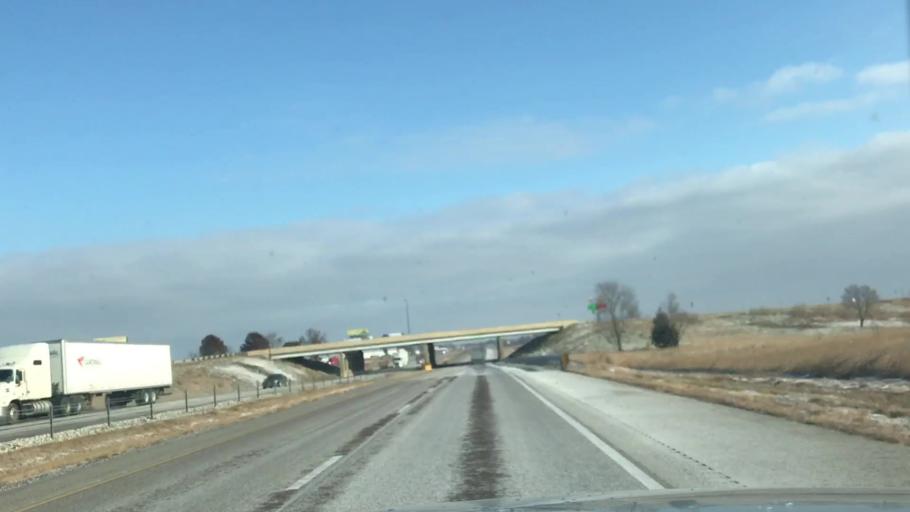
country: US
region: Illinois
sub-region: Madison County
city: Worden
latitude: 38.8876
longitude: -89.8393
